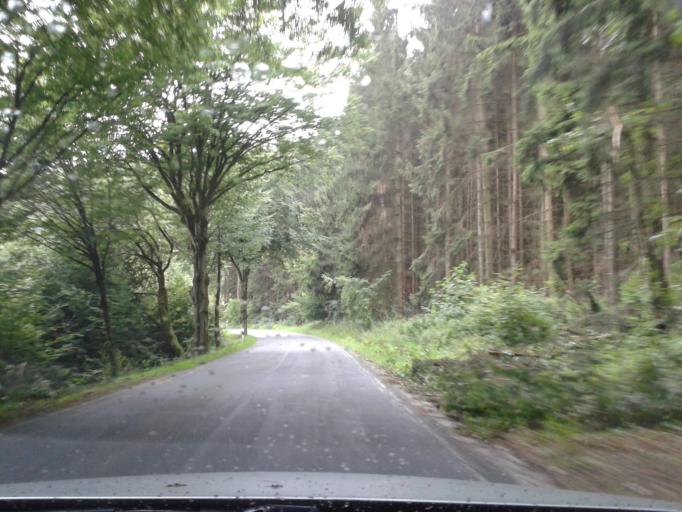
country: DE
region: North Rhine-Westphalia
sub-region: Regierungsbezirk Detmold
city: Lugde
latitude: 51.9556
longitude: 9.1938
